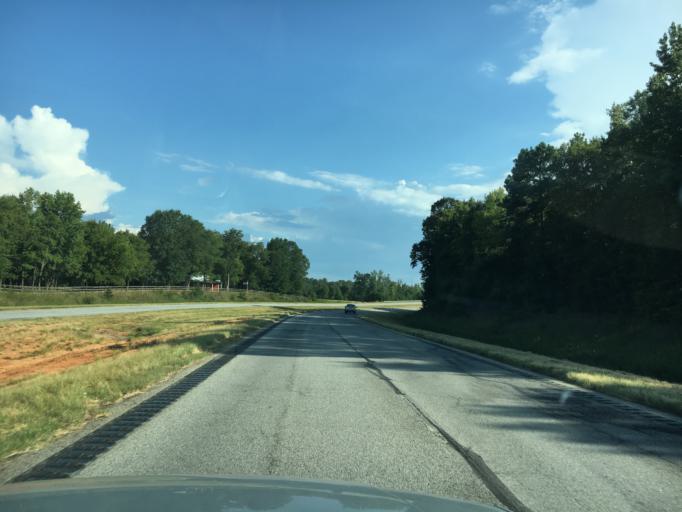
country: US
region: South Carolina
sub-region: Laurens County
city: Clinton
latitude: 34.3554
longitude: -81.9665
